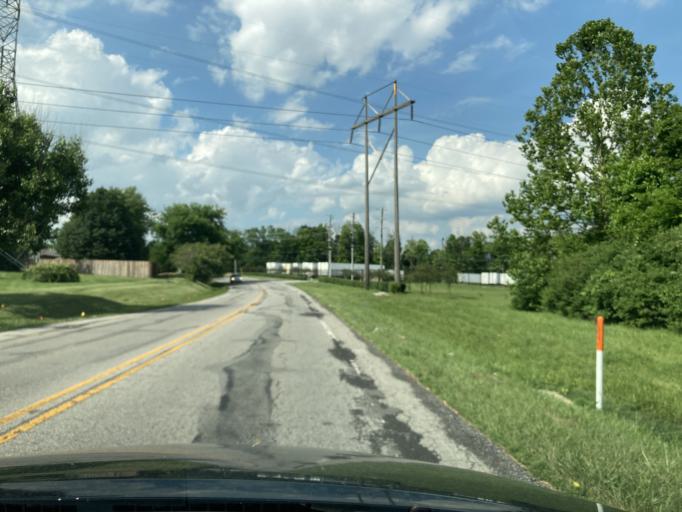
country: US
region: Indiana
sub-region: Marion County
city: Speedway
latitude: 39.8565
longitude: -86.2322
